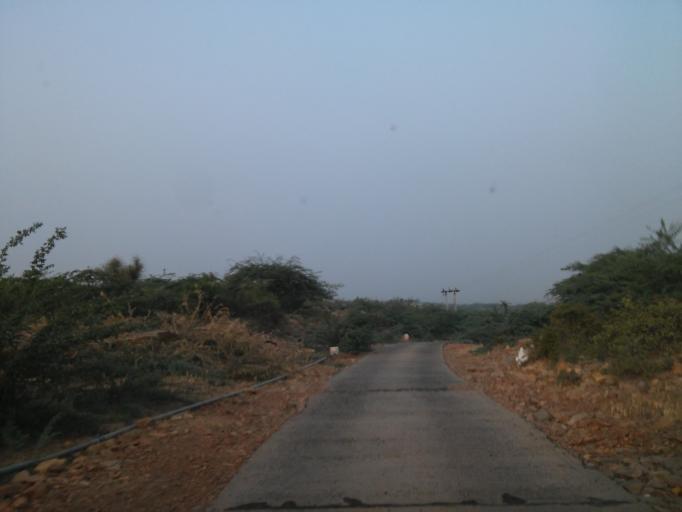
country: PK
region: Sindh
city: Diplo
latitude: 23.9218
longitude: 69.7894
